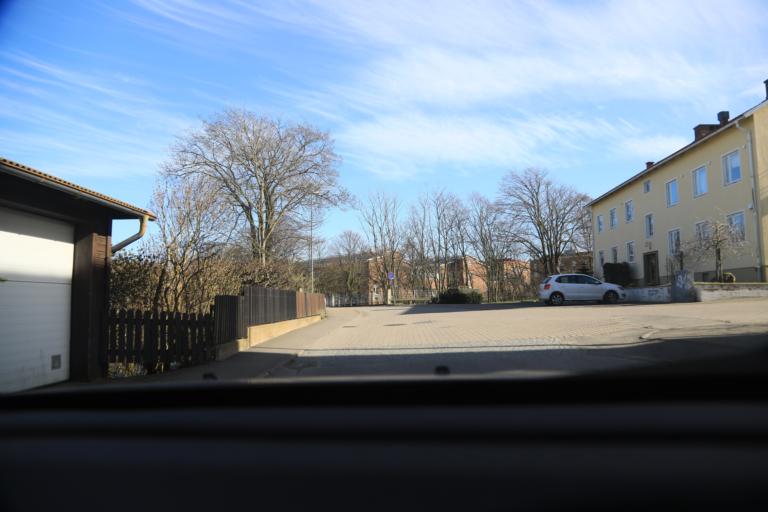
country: SE
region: Halland
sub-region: Varbergs Kommun
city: Varberg
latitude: 57.1048
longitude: 12.2453
